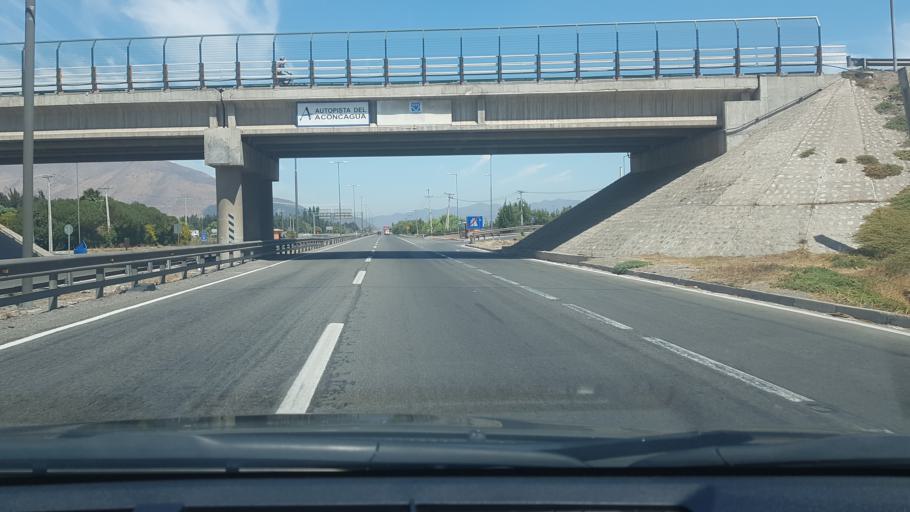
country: CL
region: Valparaiso
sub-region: Provincia de San Felipe
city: Llaillay
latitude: -32.8510
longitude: -70.9424
